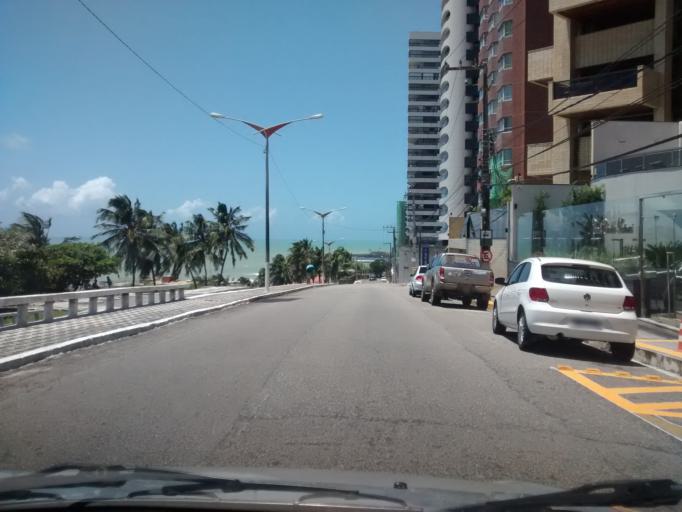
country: BR
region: Rio Grande do Norte
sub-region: Natal
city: Natal
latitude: -5.7828
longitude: -35.1942
